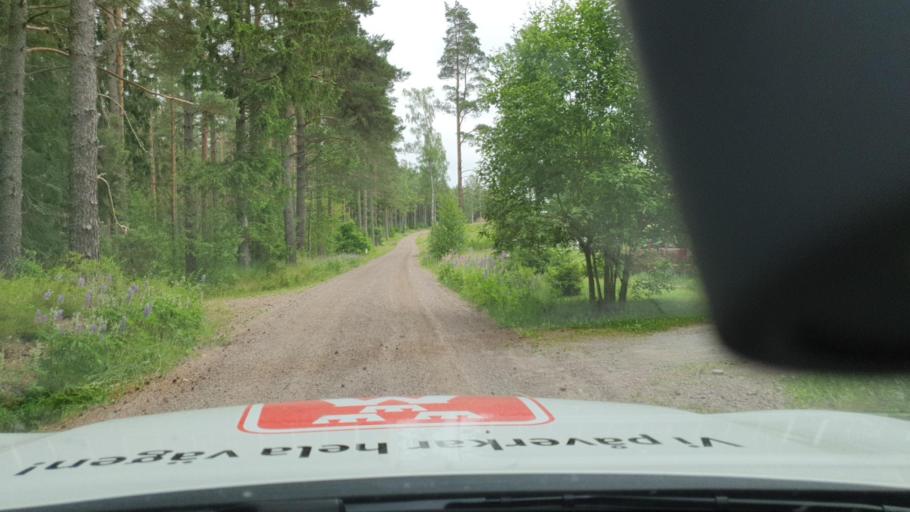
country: SE
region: Vaestra Goetaland
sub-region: Hjo Kommun
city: Hjo
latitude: 58.3996
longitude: 14.3323
